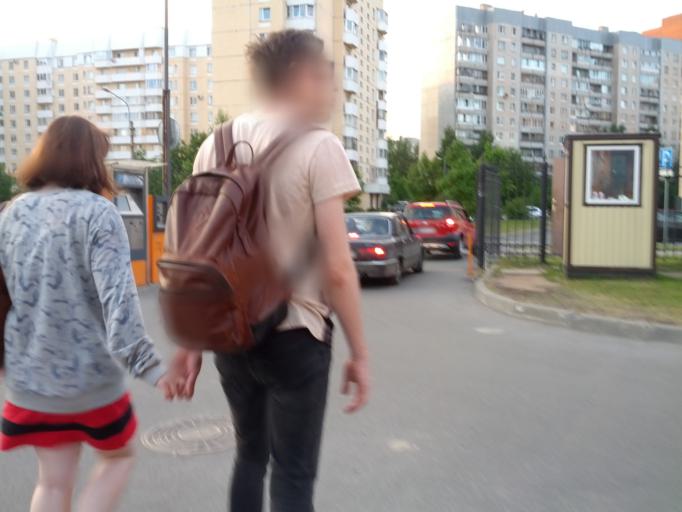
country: RU
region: Leningrad
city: Untolovo
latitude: 59.9831
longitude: 30.2095
